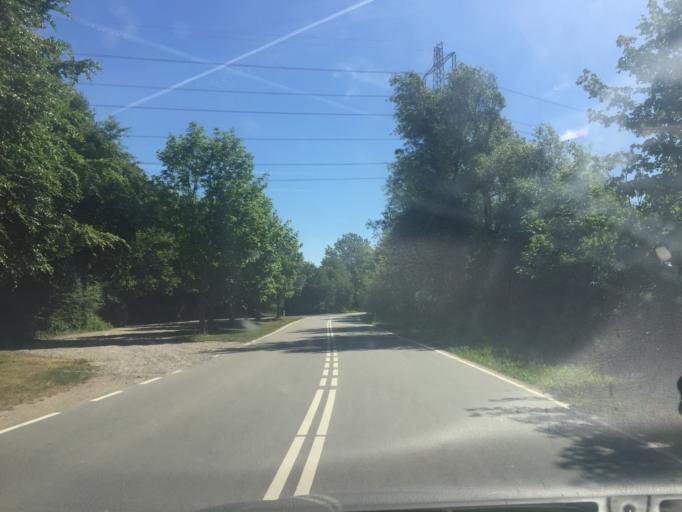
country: DK
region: Capital Region
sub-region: Hoje-Taastrup Kommune
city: Flong
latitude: 55.6676
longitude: 12.2245
